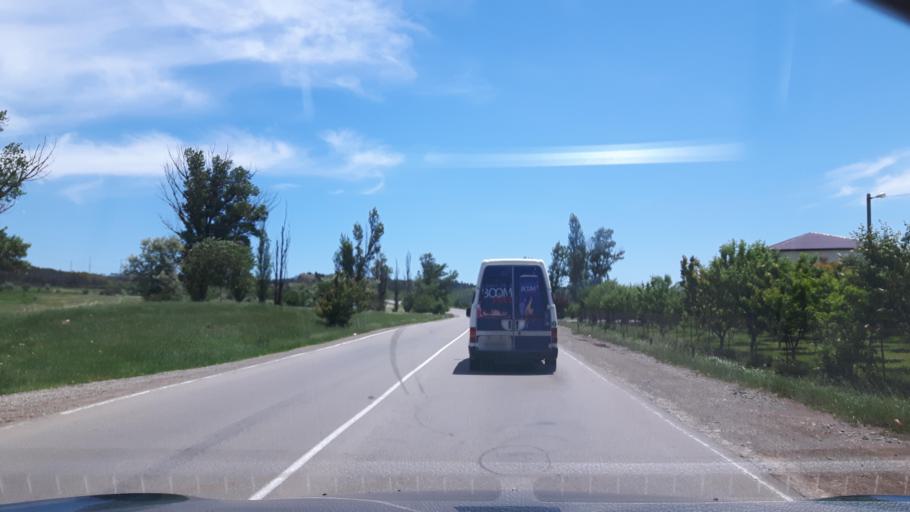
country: GE
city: Didi Lilo
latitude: 41.6932
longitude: 45.0634
